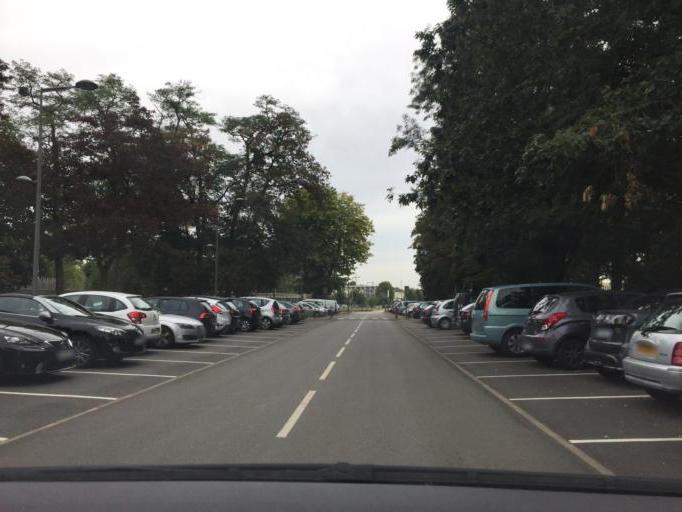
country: FR
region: Ile-de-France
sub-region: Departement des Yvelines
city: Jouy-en-Josas
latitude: 48.7556
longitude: 2.1653
